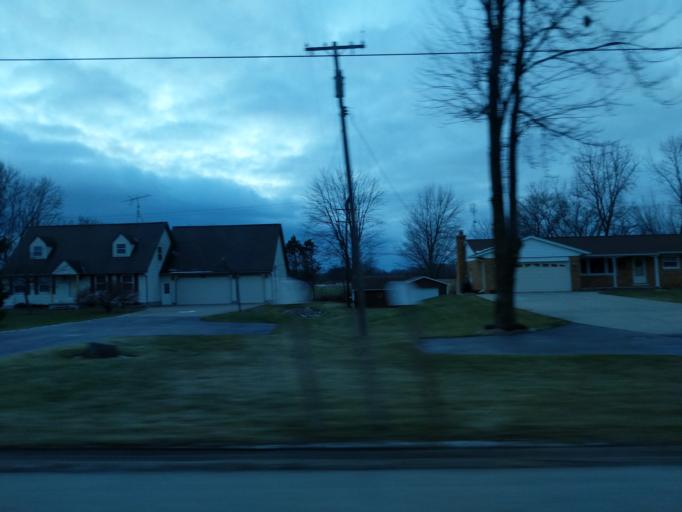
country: US
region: Michigan
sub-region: Lapeer County
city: Almont
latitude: 42.9082
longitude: -83.0445
